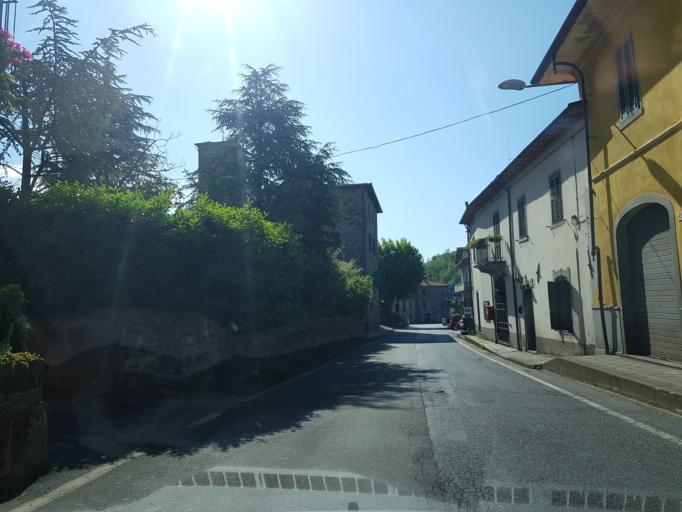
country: IT
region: Tuscany
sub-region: Provincia di Lucca
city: Piazza al Serchio-San Michele
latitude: 44.1837
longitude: 10.3004
